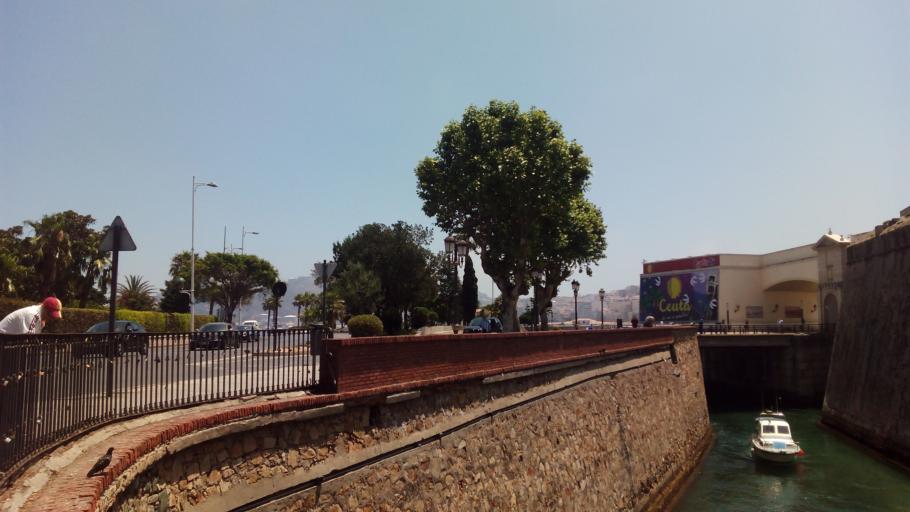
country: ES
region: Ceuta
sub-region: Ceuta
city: Ceuta
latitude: 35.8900
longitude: -5.3190
